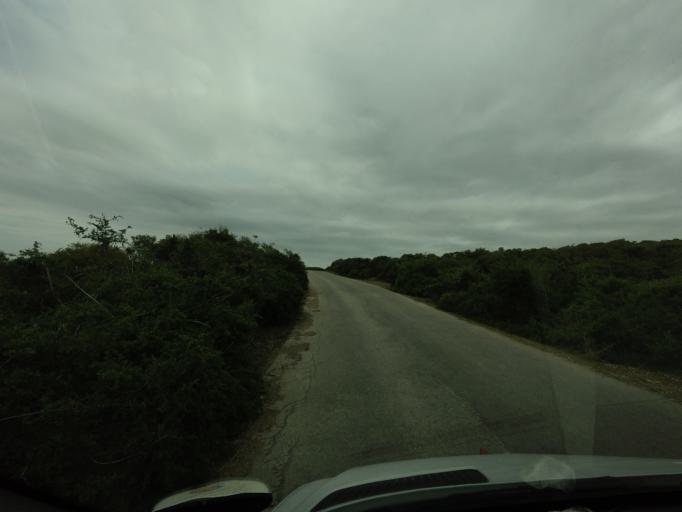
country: ZA
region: Eastern Cape
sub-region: Cacadu District Municipality
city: Kirkwood
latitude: -33.4687
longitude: 25.7702
